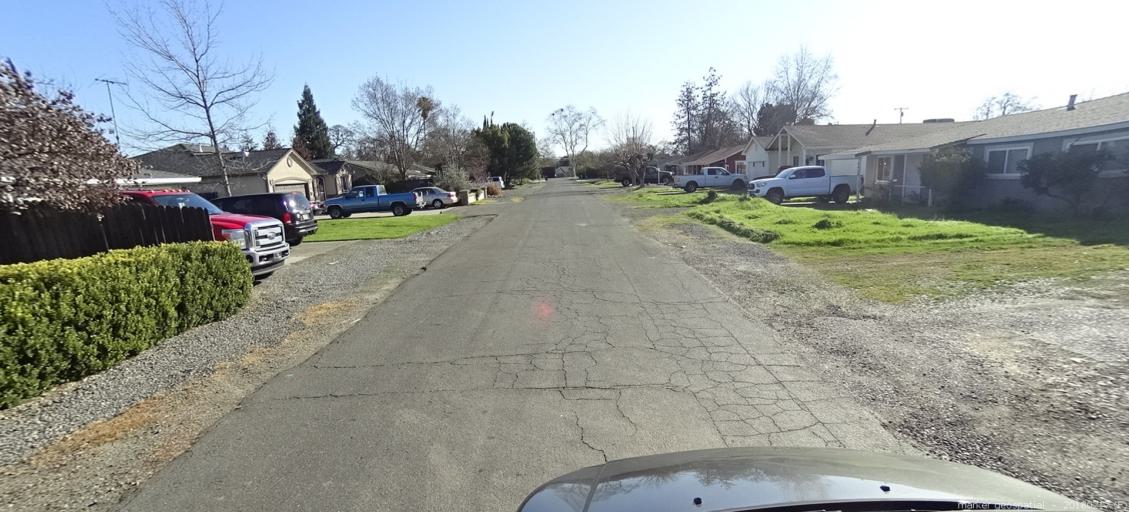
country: US
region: California
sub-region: Sacramento County
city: Folsom
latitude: 38.6703
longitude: -121.1993
